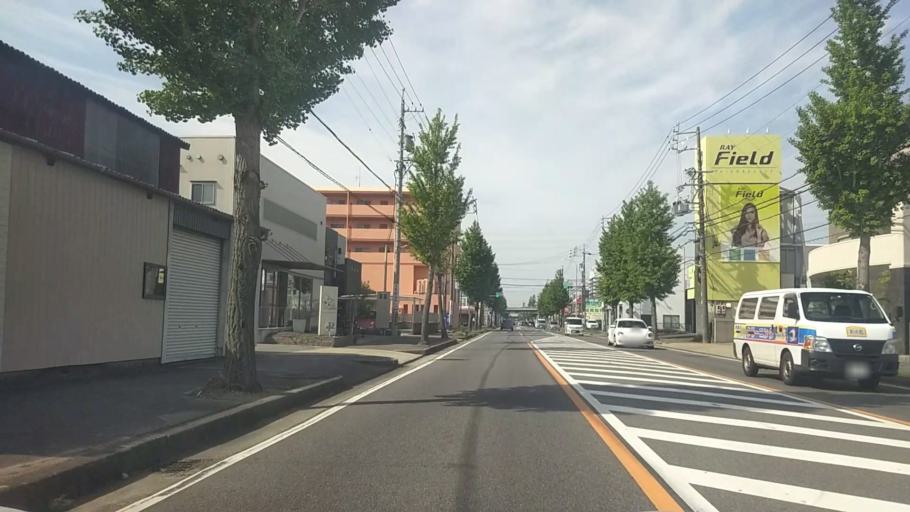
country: JP
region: Aichi
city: Okazaki
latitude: 34.9441
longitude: 137.1537
